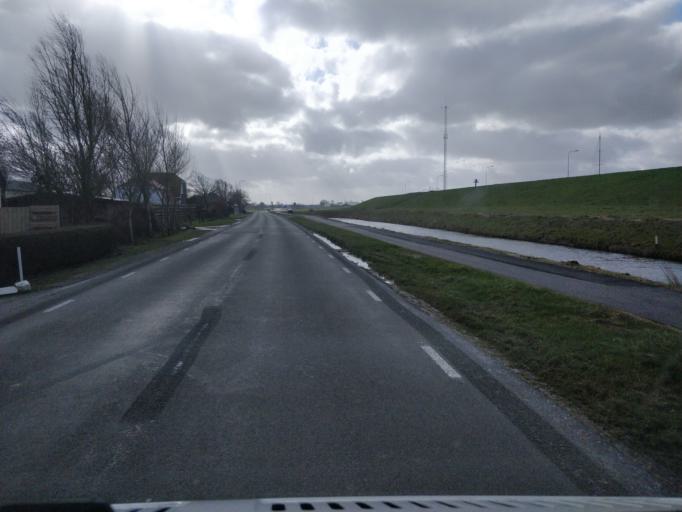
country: NL
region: Friesland
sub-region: Gemeente Harlingen
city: Harlingen
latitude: 53.1911
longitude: 5.4416
